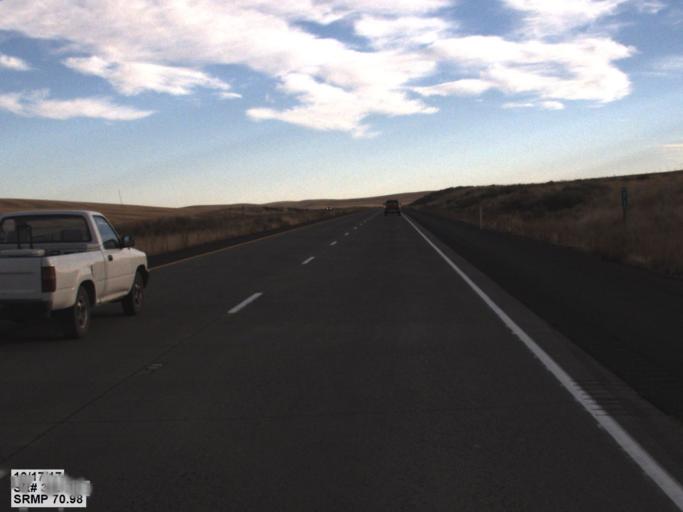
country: US
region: Washington
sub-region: Franklin County
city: Connell
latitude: 46.8261
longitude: -118.6678
